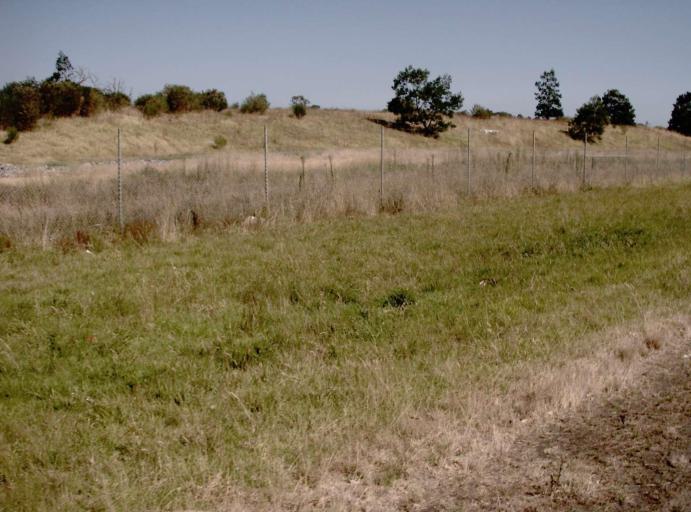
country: AU
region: Victoria
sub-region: Frankston
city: Sandhurst
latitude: -38.0774
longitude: 145.1906
